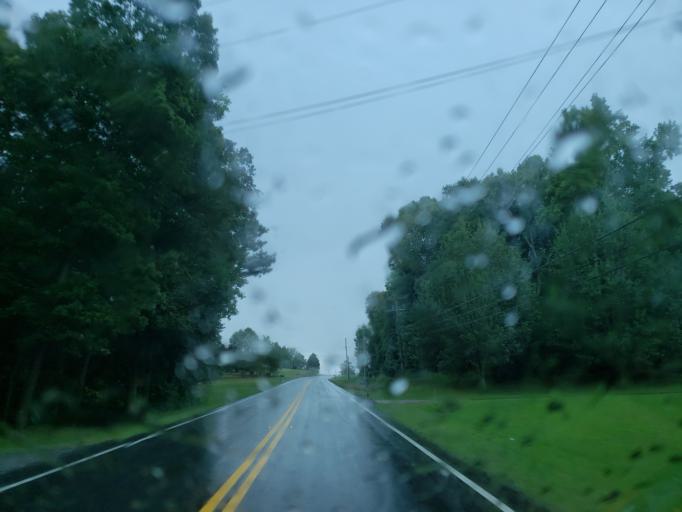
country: US
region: Georgia
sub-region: Cherokee County
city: Canton
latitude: 34.3177
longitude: -84.4654
